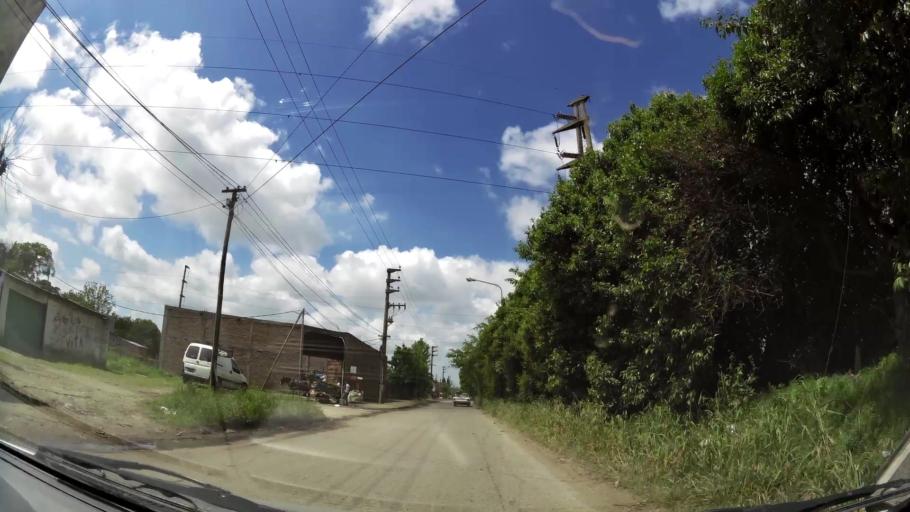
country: AR
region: Buenos Aires
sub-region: Partido de Quilmes
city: Quilmes
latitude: -34.8395
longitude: -58.2364
